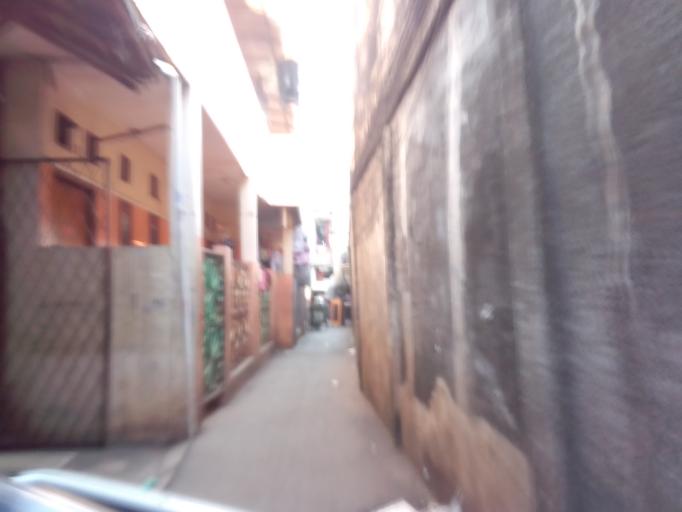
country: ID
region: Jakarta Raya
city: Jakarta
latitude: -6.2658
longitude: 106.8114
